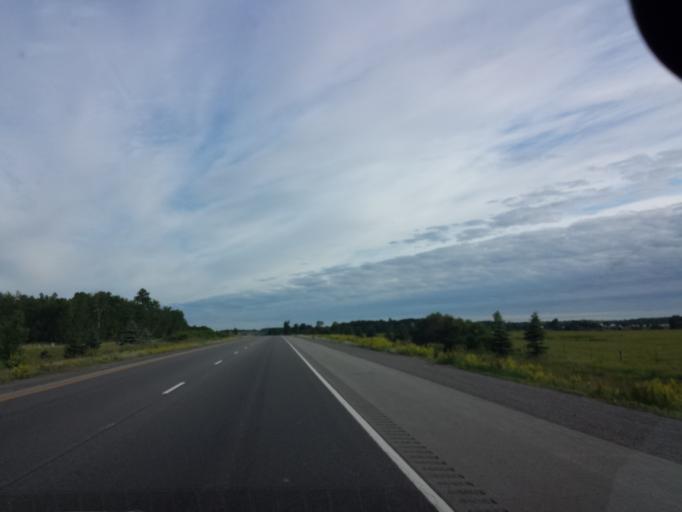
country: CA
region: Ontario
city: Arnprior
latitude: 45.3842
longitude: -76.2620
